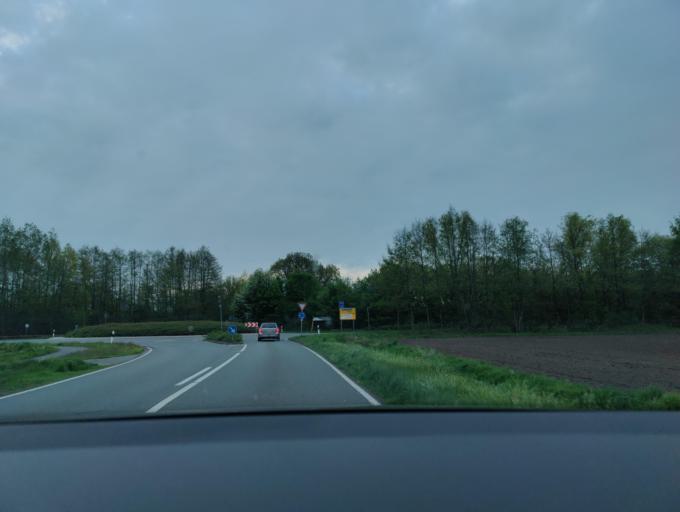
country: DE
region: Lower Saxony
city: Wietmarschen
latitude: 52.4945
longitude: 7.2118
